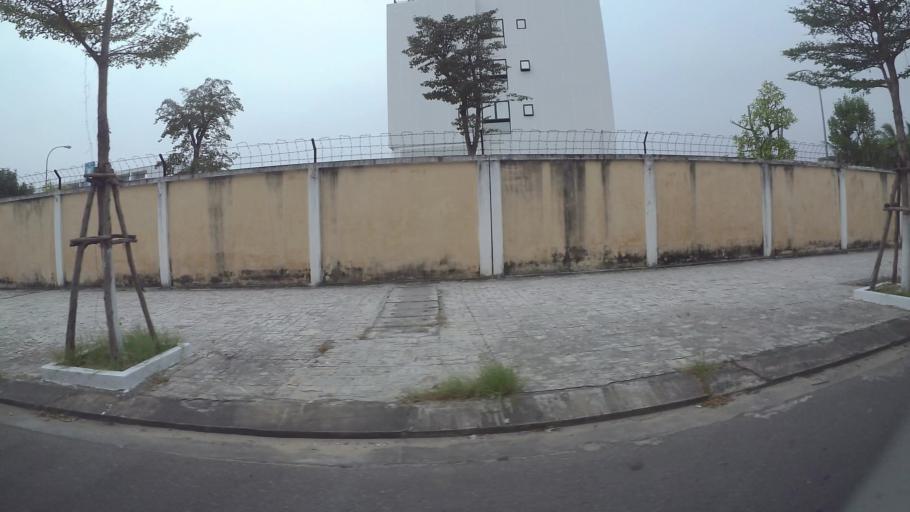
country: VN
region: Da Nang
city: Cam Le
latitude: 16.0394
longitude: 108.2096
